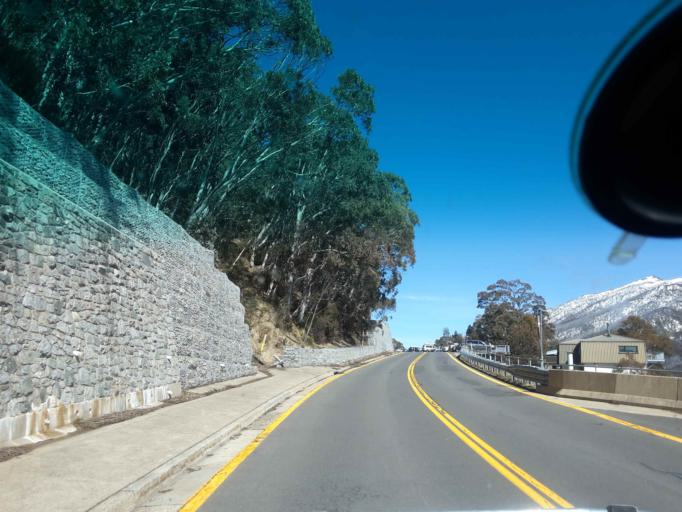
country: AU
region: New South Wales
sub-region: Snowy River
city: Jindabyne
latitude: -36.5039
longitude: 148.3095
